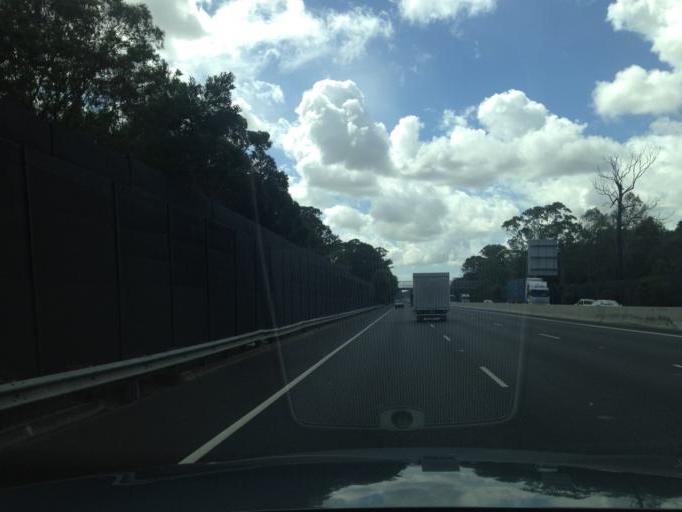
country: AU
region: New South Wales
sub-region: Bankstown
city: Padstow
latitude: -33.9414
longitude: 151.0445
